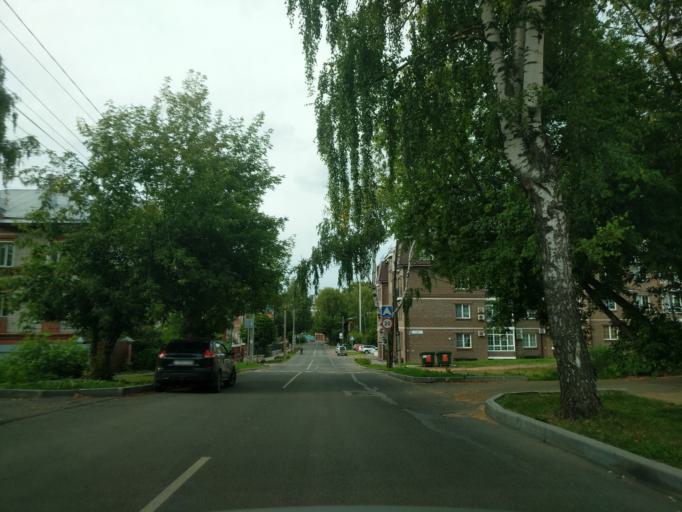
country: RU
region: Kirov
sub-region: Kirovo-Chepetskiy Rayon
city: Kirov
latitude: 58.5976
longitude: 49.6881
